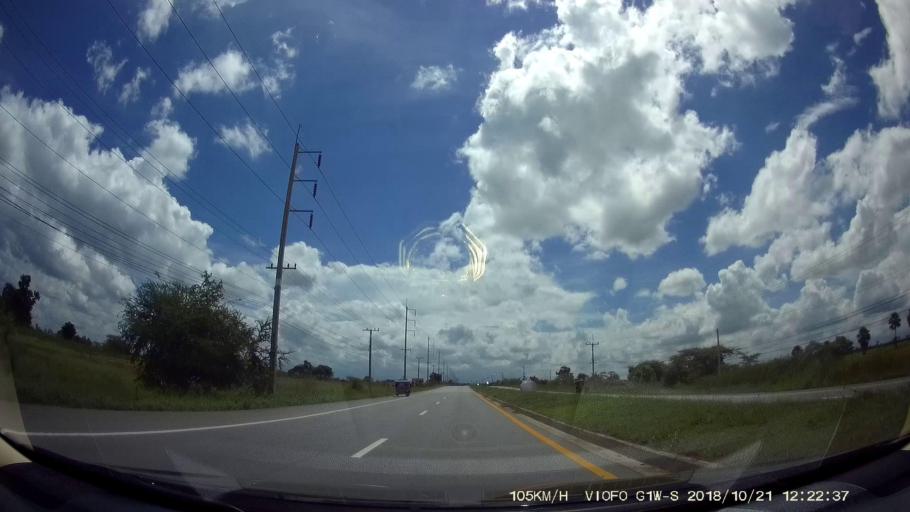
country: TH
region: Nakhon Ratchasima
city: Dan Khun Thot
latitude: 15.2584
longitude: 101.7894
